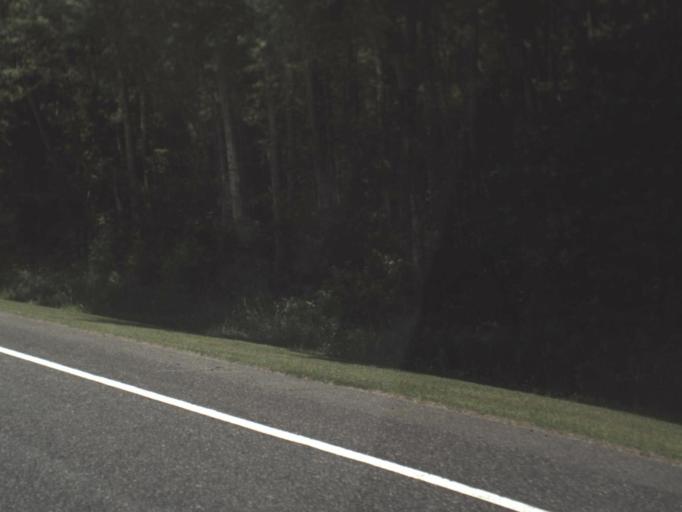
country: US
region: Florida
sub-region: Columbia County
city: Watertown
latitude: 30.2542
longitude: -82.4080
